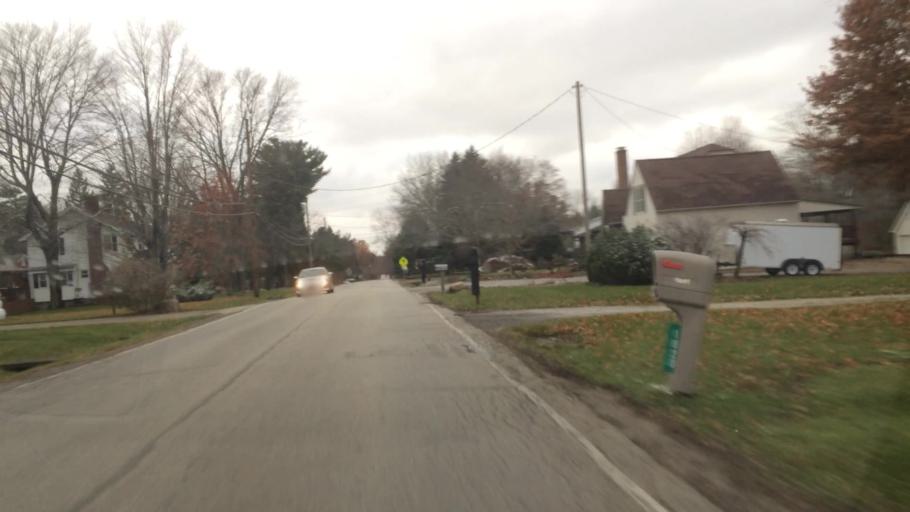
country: US
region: Ohio
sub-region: Summit County
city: Stow
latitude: 41.1750
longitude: -81.4428
